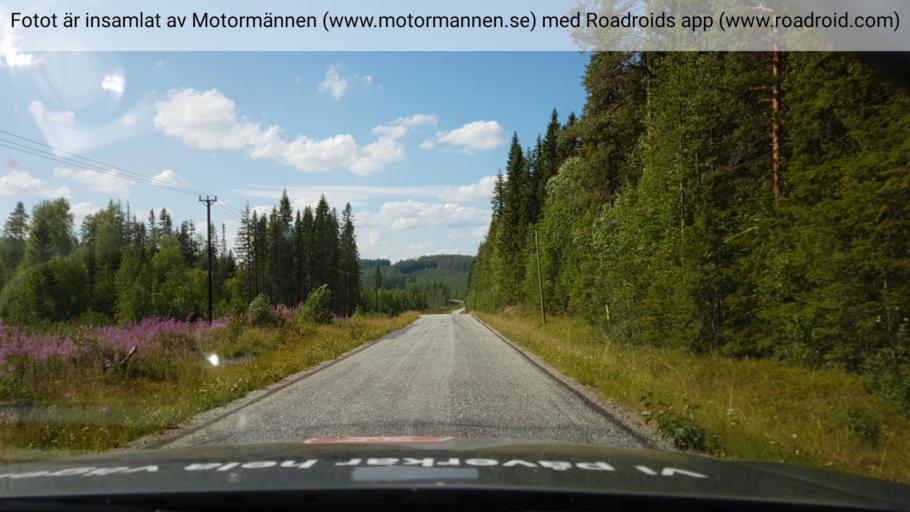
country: SE
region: Vaesterbotten
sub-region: Dorotea Kommun
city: Dorotea
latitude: 64.1263
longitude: 16.2727
